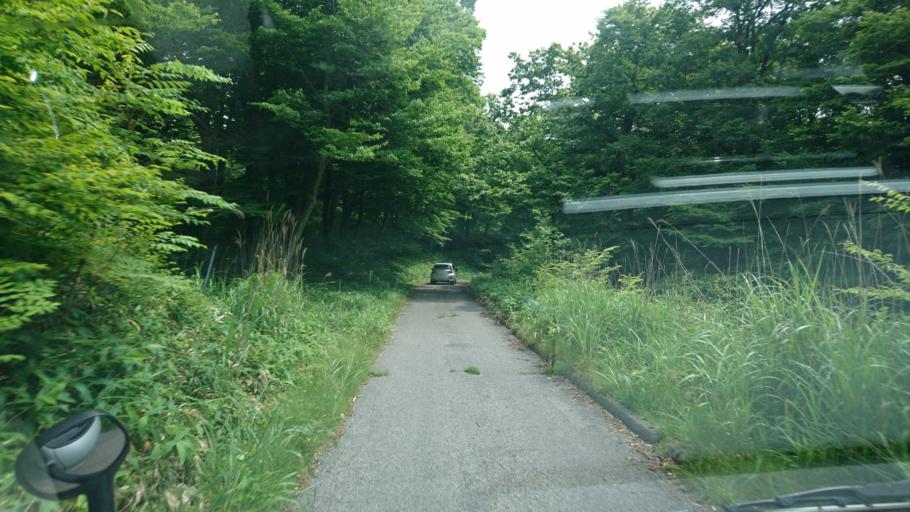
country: JP
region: Iwate
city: Ofunato
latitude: 39.1762
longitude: 141.7701
